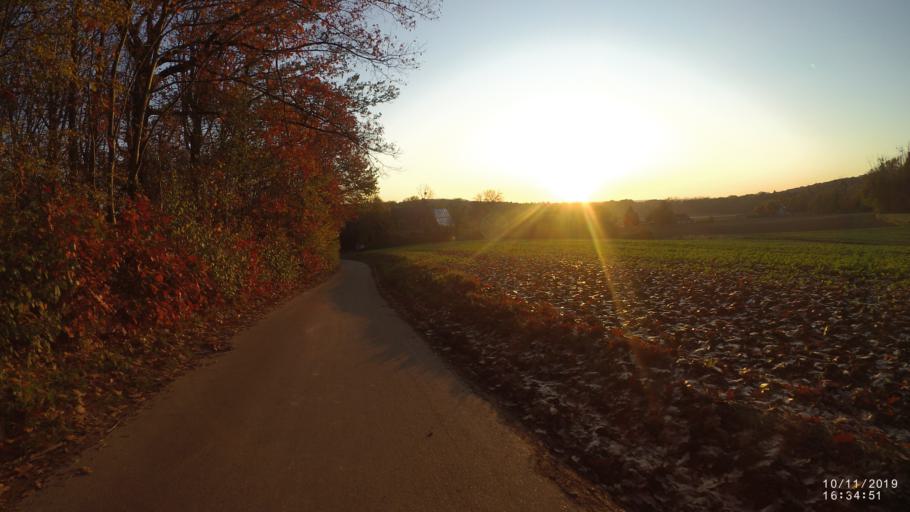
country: BE
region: Flanders
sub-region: Provincie Vlaams-Brabant
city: Bierbeek
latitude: 50.8698
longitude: 4.7889
